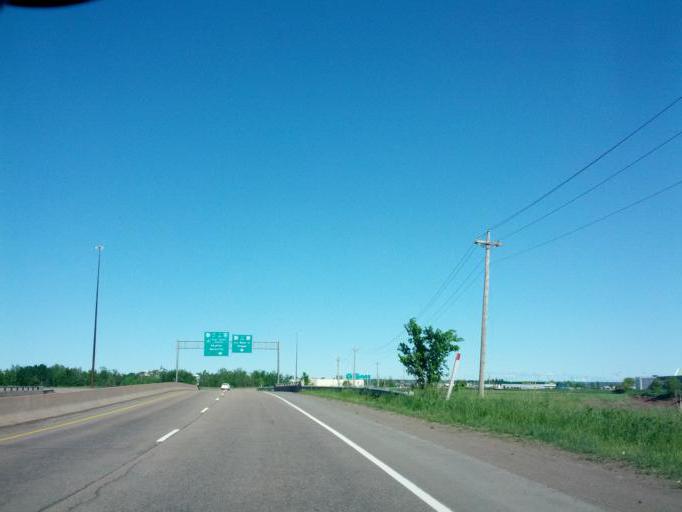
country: CA
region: New Brunswick
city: Moncton
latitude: 46.0971
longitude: -64.7729
